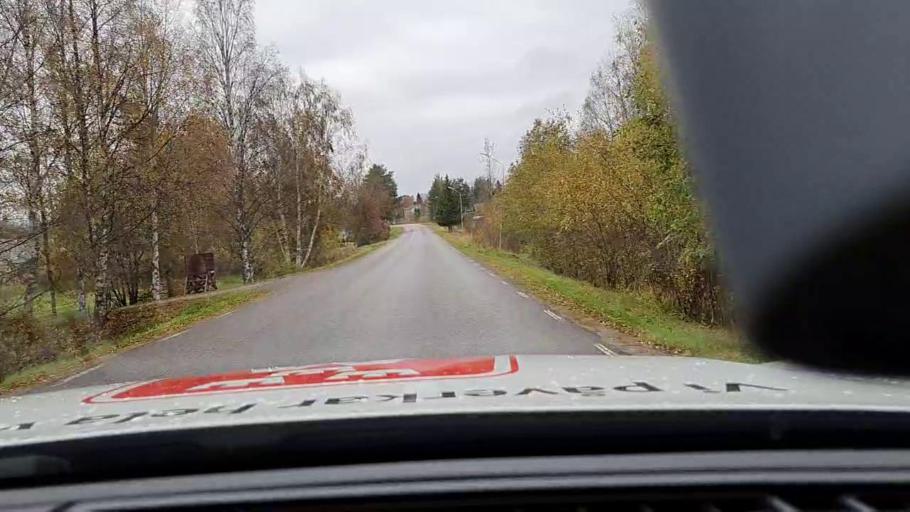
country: SE
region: Norrbotten
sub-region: Haparanda Kommun
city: Haparanda
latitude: 65.8008
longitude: 23.9193
